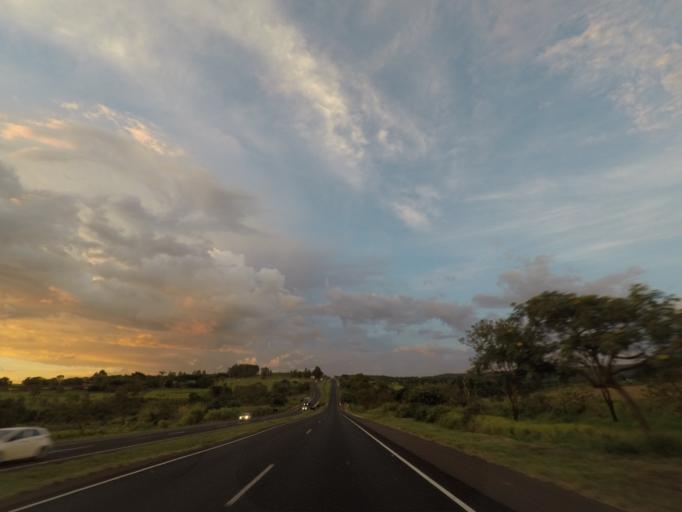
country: BR
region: Minas Gerais
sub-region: Uberaba
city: Uberaba
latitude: -19.6107
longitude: -48.0211
